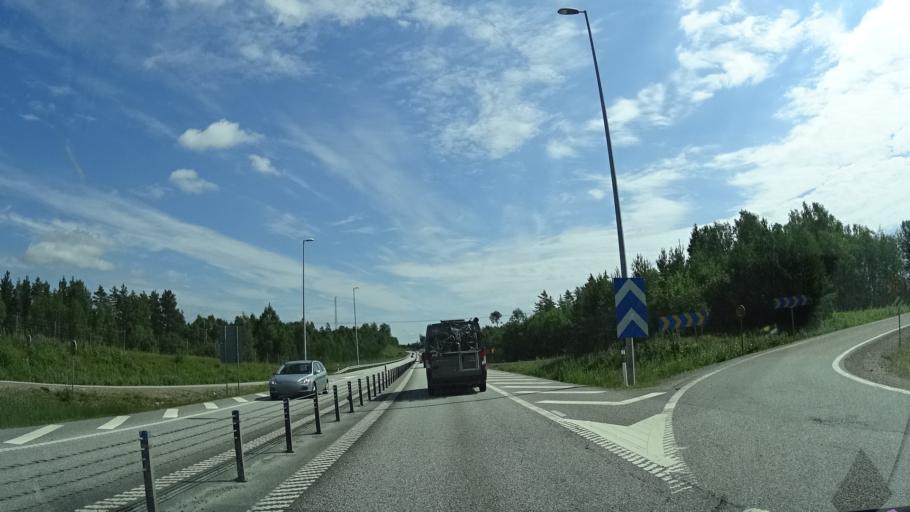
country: SE
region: OErebro
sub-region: Degerfors Kommun
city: Degerfors
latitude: 59.3214
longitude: 14.3969
